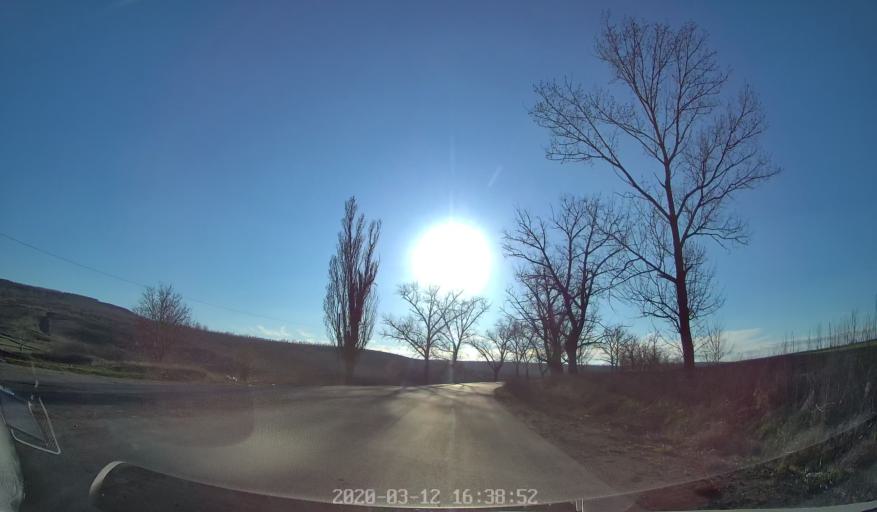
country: MD
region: Anenii Noi
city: Anenii Noi
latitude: 46.8144
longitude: 29.1744
